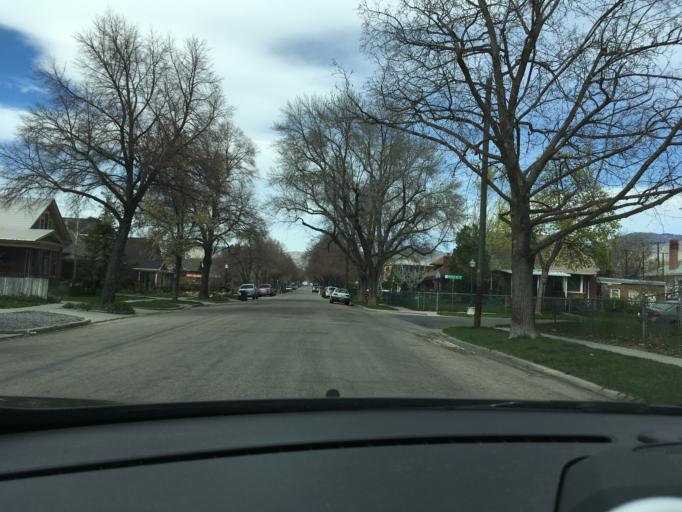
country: US
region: Utah
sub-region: Salt Lake County
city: South Salt Lake
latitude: 40.7368
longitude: -111.8625
